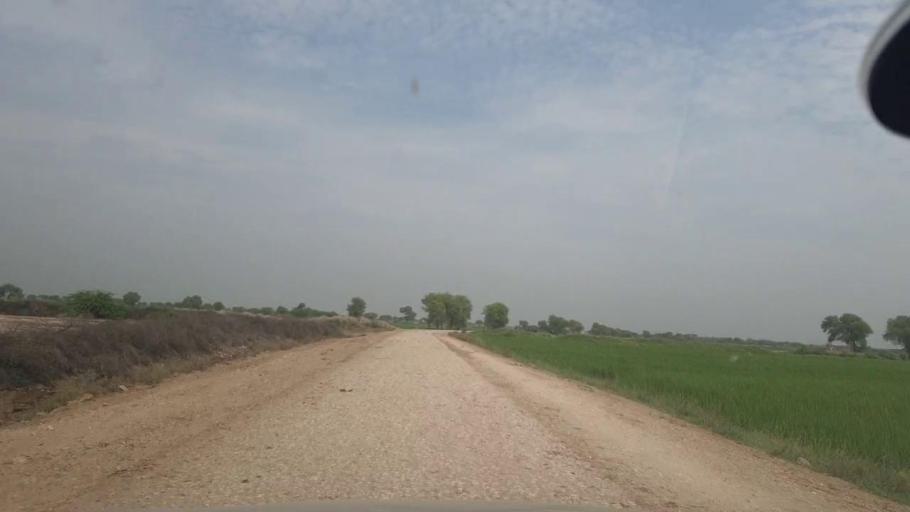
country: PK
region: Sindh
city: Jacobabad
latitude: 28.2441
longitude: 68.5418
